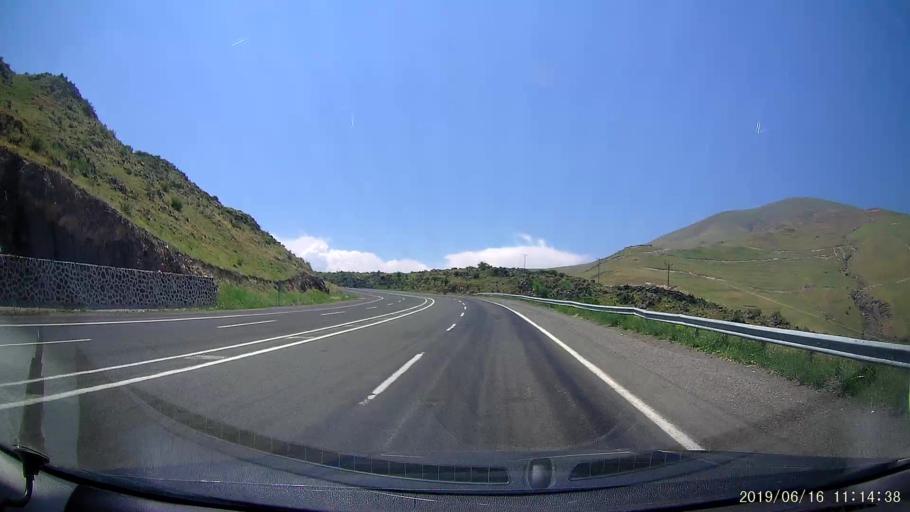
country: TR
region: Igdir
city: Igdir
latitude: 39.7757
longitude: 44.1418
